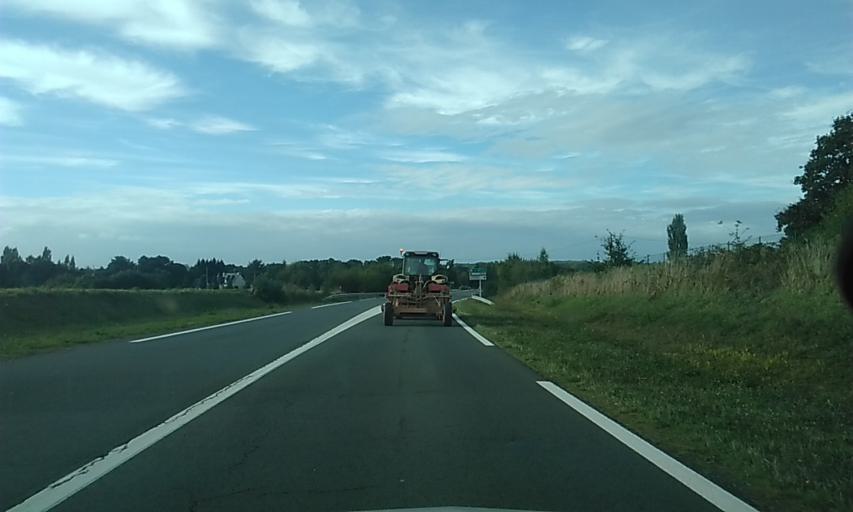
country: FR
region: Brittany
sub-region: Departement d'Ille-et-Vilaine
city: Bedee
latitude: 48.1860
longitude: -1.9398
